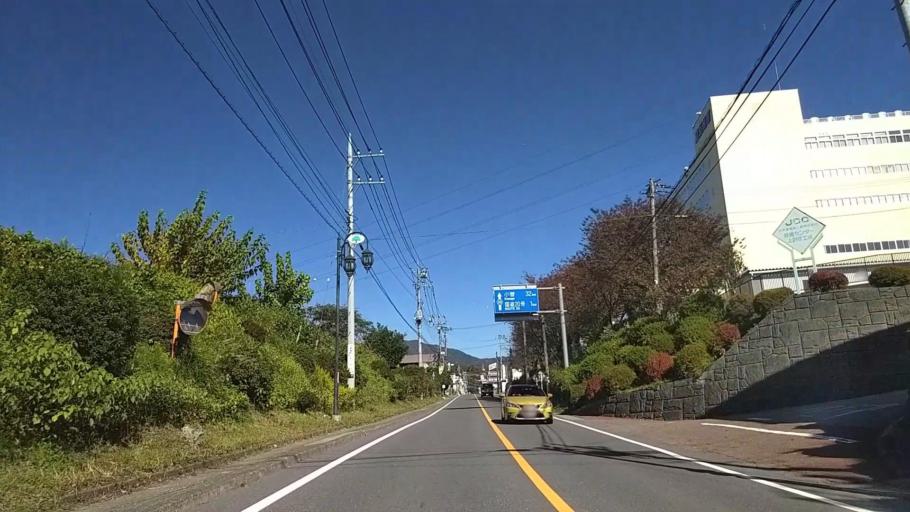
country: JP
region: Yamanashi
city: Uenohara
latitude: 35.6204
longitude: 139.1122
